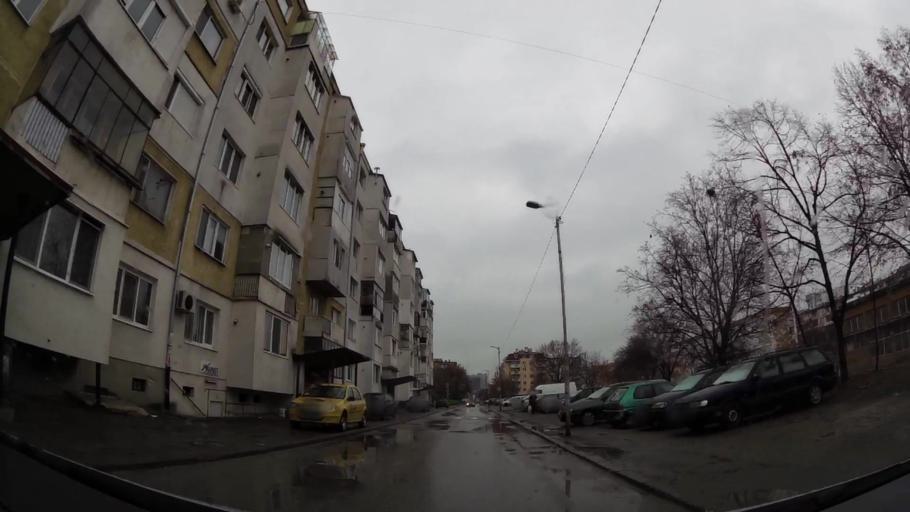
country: BG
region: Sofia-Capital
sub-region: Stolichna Obshtina
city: Sofia
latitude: 42.6656
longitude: 23.3968
